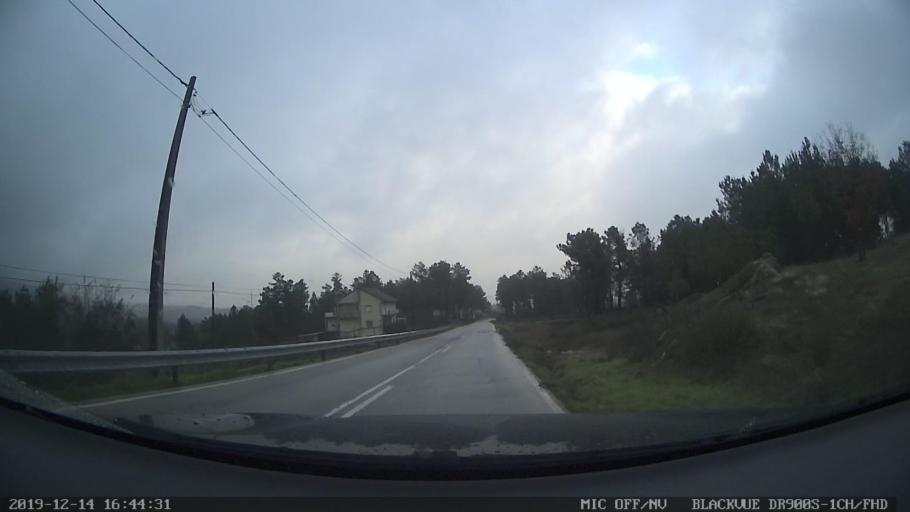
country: PT
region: Vila Real
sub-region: Murca
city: Murca
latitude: 41.3923
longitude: -7.4948
